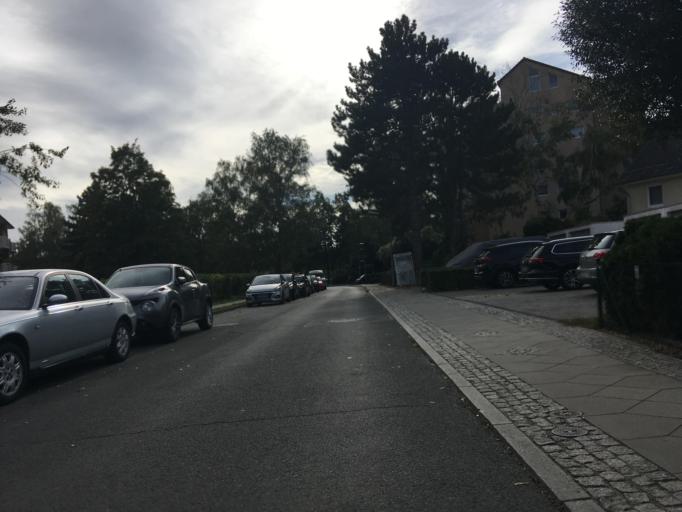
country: DE
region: Berlin
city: Britz
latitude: 52.4252
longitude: 13.4292
